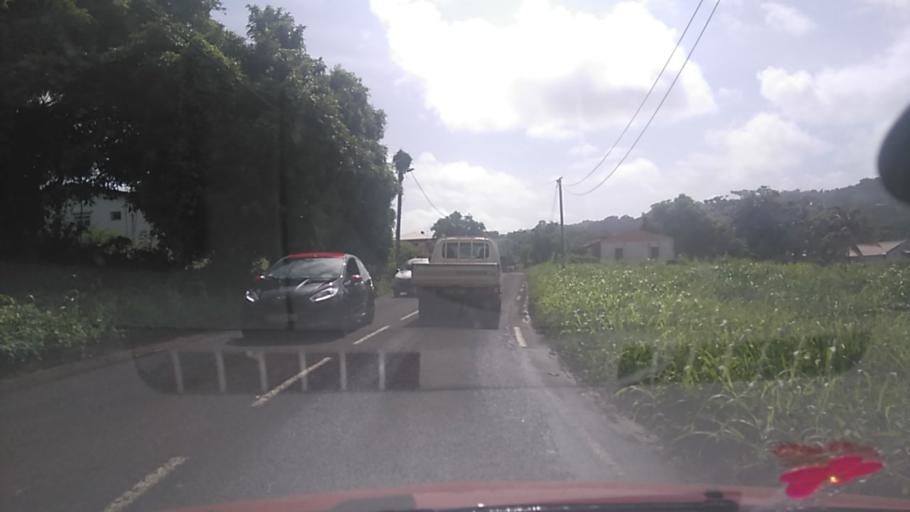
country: MQ
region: Martinique
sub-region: Martinique
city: Saint-Esprit
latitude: 14.5803
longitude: -60.9281
